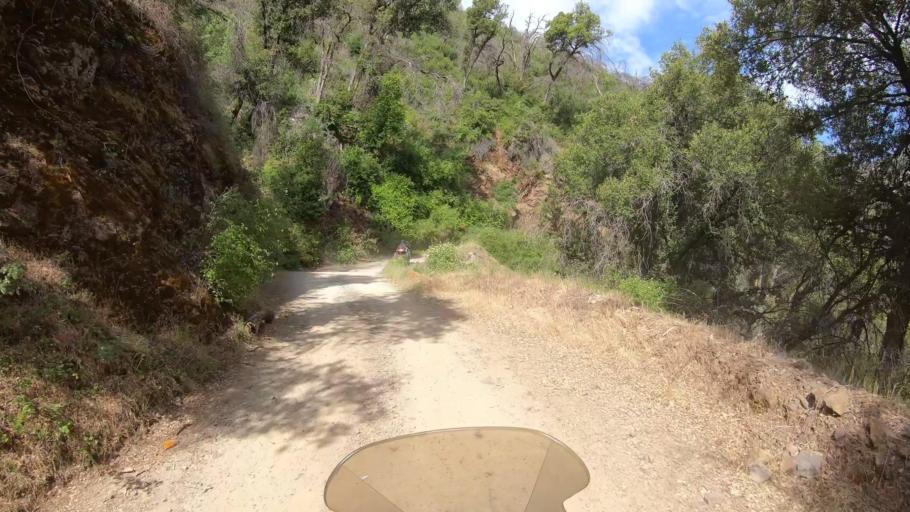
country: US
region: California
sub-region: Tuolumne County
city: Tuolumne City
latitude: 37.8339
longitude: -120.0684
